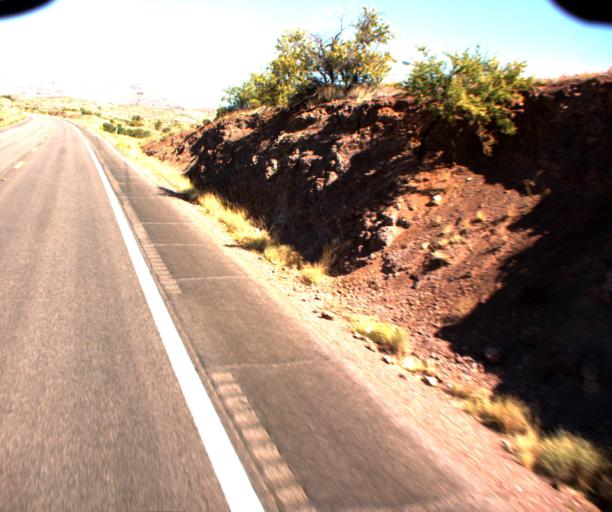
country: US
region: Arizona
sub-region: Greenlee County
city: Clifton
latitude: 32.7654
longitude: -109.2526
